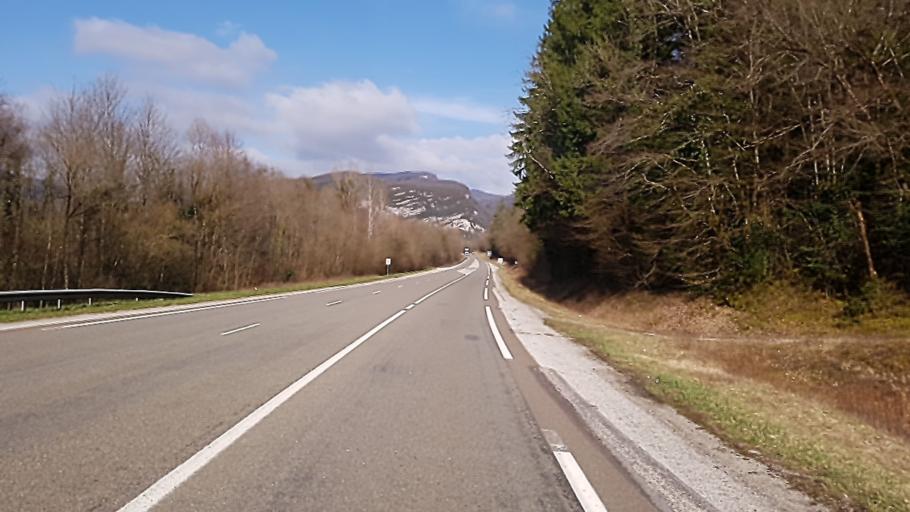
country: FR
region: Rhone-Alpes
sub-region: Departement de l'Ain
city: Dortan
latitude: 46.3585
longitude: 5.7000
